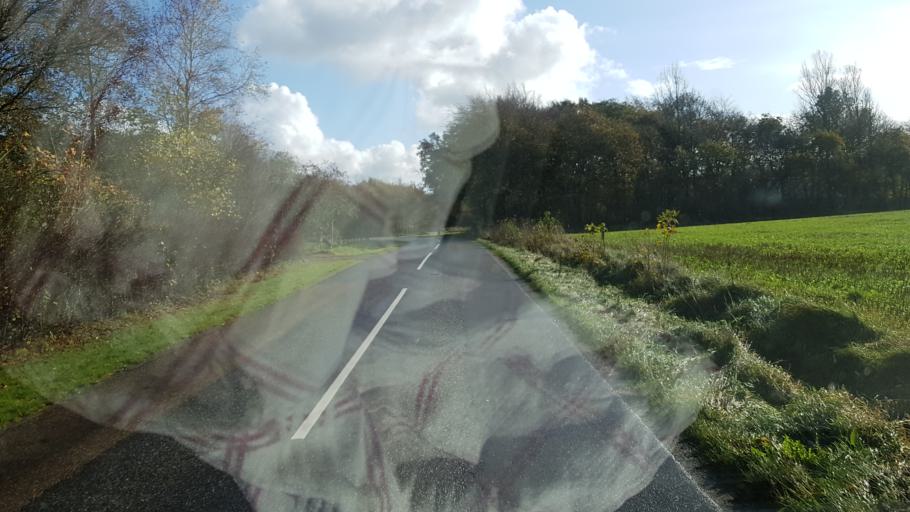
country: DK
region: South Denmark
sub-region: Varde Kommune
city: Olgod
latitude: 55.6904
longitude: 8.6589
